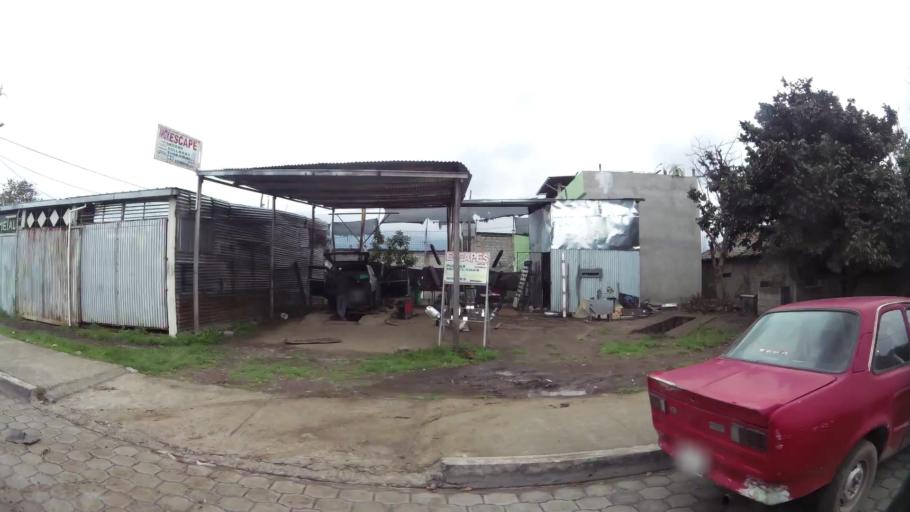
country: EC
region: Pichincha
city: Sangolqui
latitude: -0.3360
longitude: -78.4649
